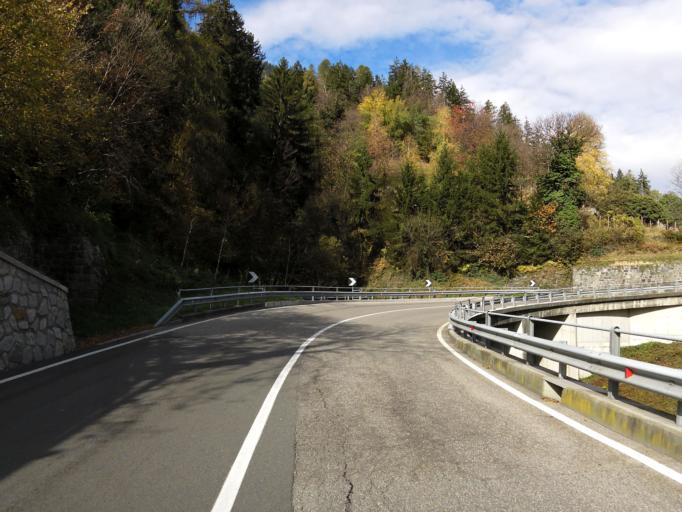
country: IT
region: Trentino-Alto Adige
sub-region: Bolzano
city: Rifiano
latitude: 46.7147
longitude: 11.1892
